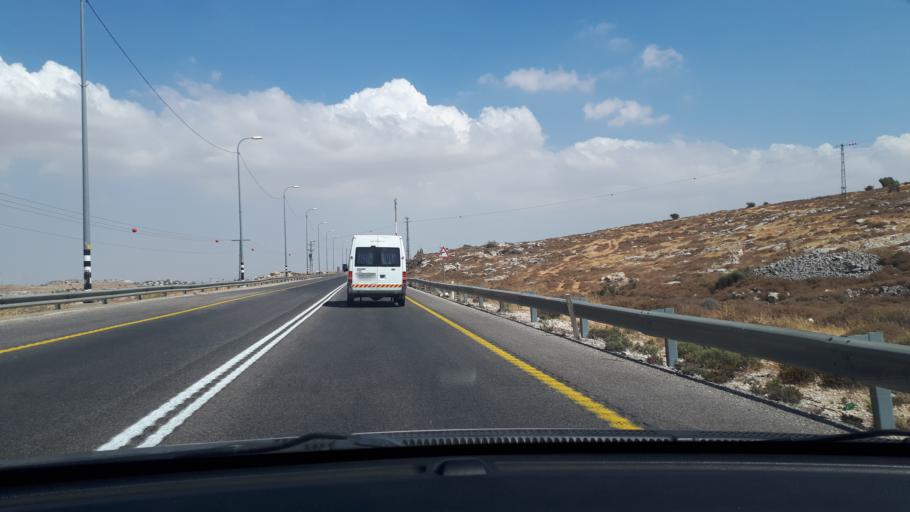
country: PS
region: West Bank
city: Dayr Dibwan
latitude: 31.8931
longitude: 35.2732
